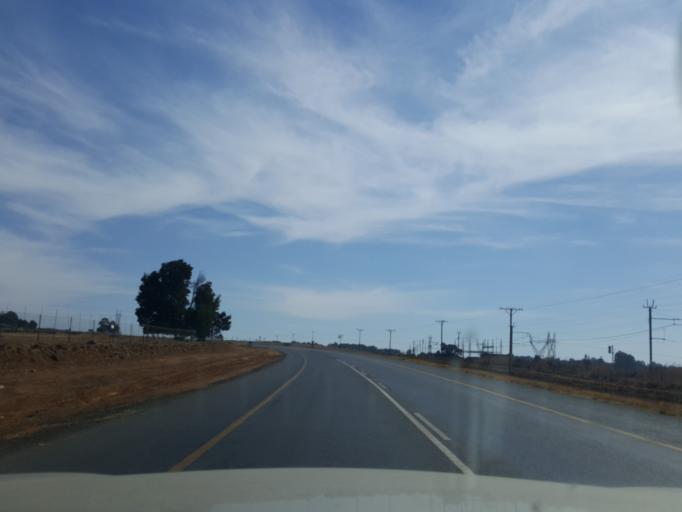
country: ZA
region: Mpumalanga
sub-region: Nkangala District Municipality
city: Belfast
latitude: -25.7171
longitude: 30.0759
